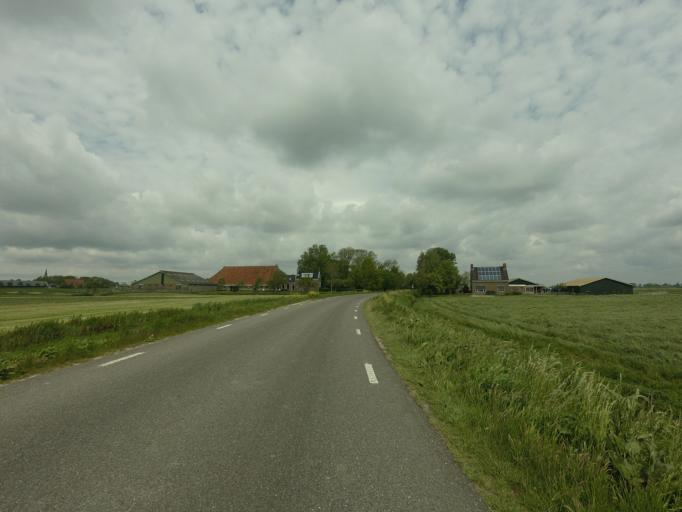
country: NL
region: Friesland
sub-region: Sudwest Fryslan
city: Bolsward
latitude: 53.1039
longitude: 5.5405
